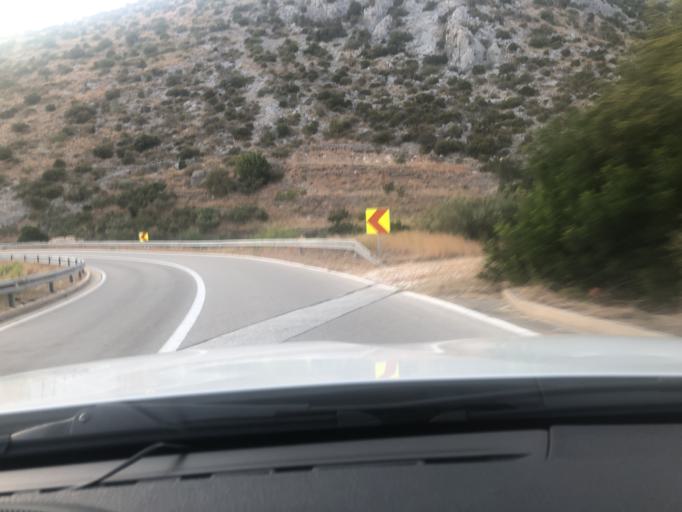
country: HR
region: Splitsko-Dalmatinska
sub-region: Grad Hvar
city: Hvar
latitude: 43.1576
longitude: 16.5081
